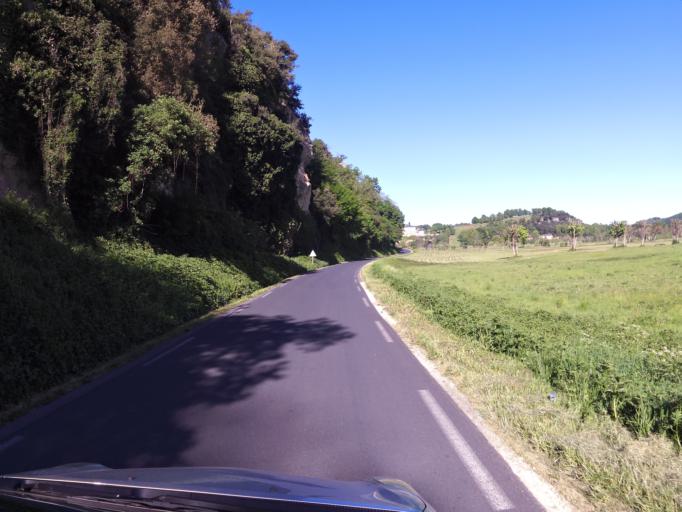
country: FR
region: Aquitaine
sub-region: Departement de la Dordogne
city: Carsac-Aillac
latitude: 44.8296
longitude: 1.2293
